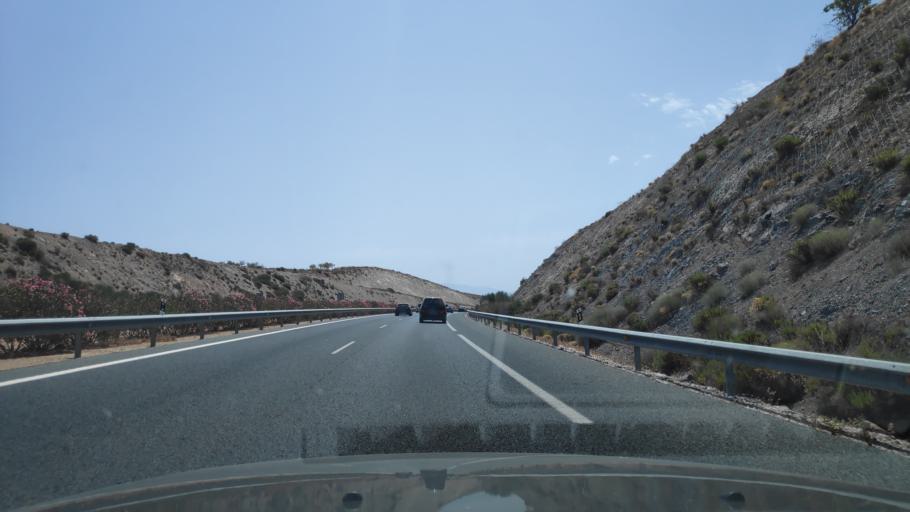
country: ES
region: Andalusia
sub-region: Provincia de Granada
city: Padul
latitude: 37.0026
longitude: -3.6335
